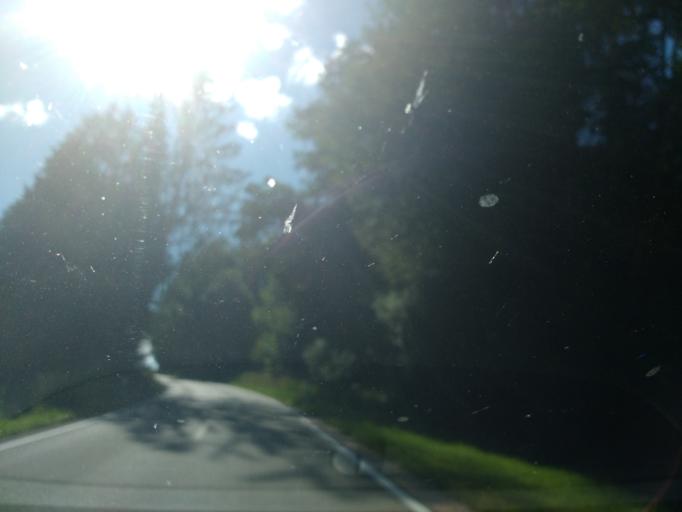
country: DE
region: Bavaria
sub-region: Upper Bavaria
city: Engelsberg
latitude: 48.1237
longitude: 12.5101
